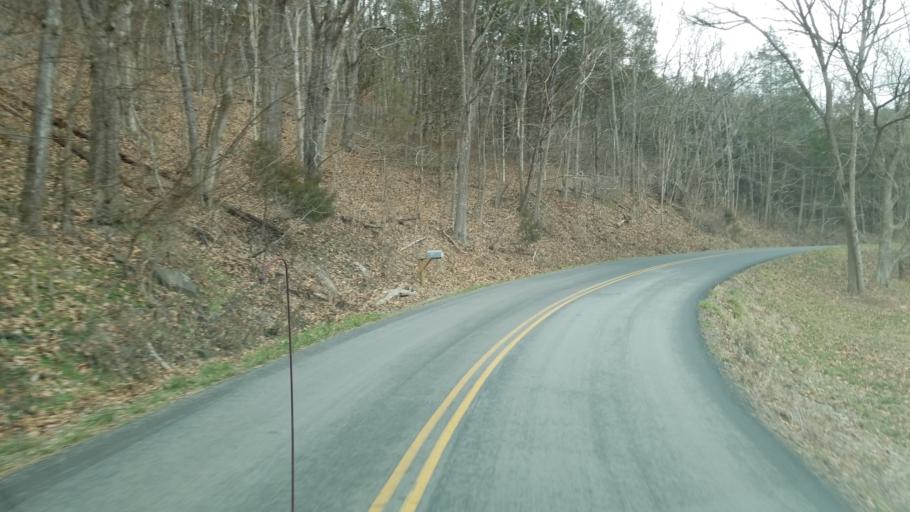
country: US
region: Virginia
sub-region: Giles County
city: Pearisburg
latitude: 37.2425
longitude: -80.7042
